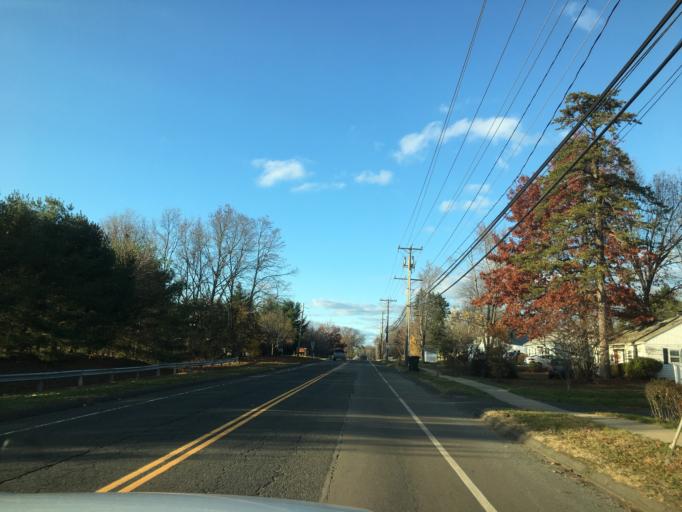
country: US
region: Connecticut
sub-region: Hartford County
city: Windsor Locks
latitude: 41.9169
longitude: -72.6612
